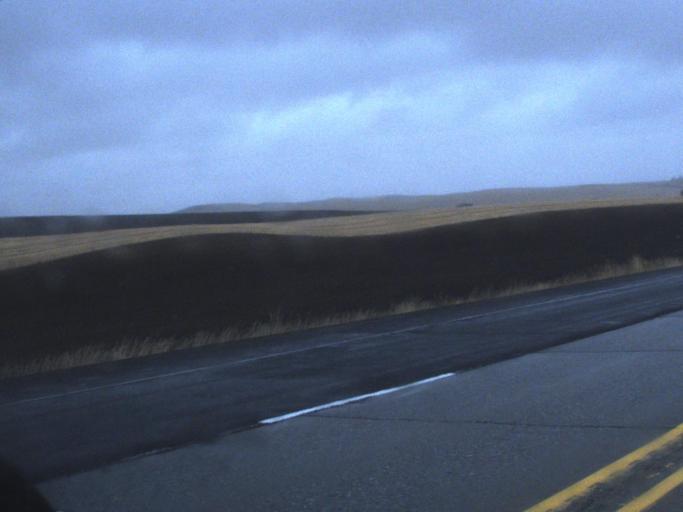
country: US
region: Washington
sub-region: Whitman County
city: Colfax
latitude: 47.2009
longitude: -117.3670
